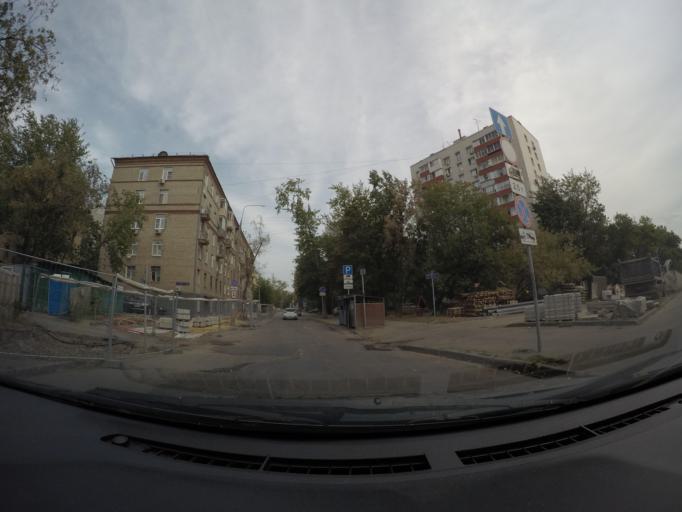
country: RU
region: Moscow
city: Sokol'niki
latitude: 55.7843
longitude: 37.6842
